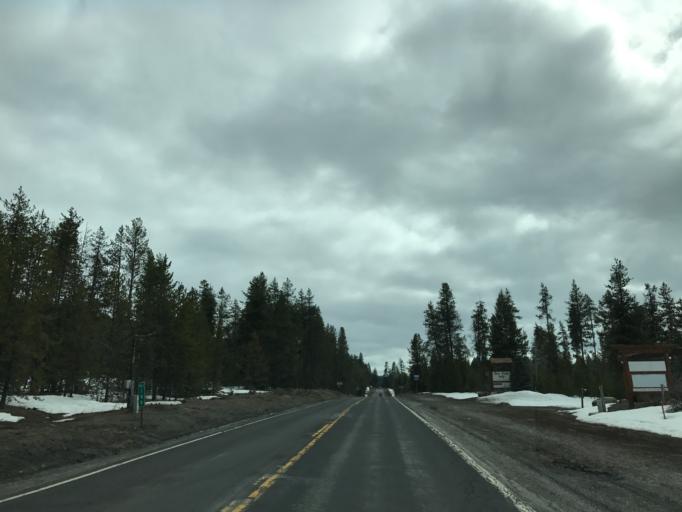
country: US
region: Idaho
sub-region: Valley County
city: McCall
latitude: 44.9501
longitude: -116.1689
